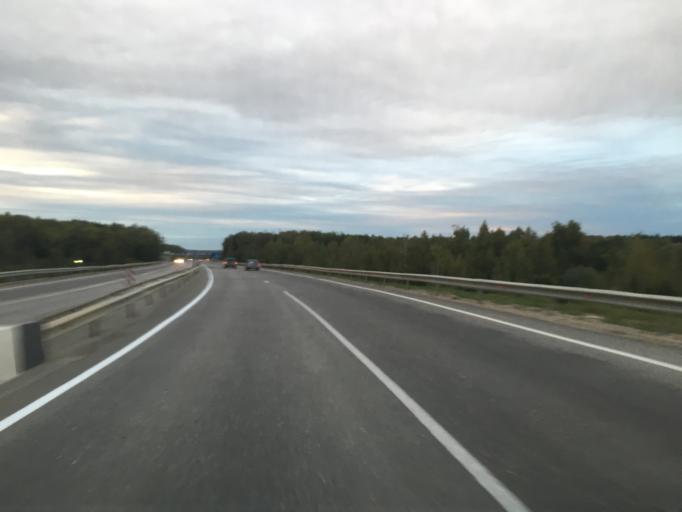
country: RU
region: Kaluga
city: Kaluga
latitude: 54.5832
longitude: 36.3362
